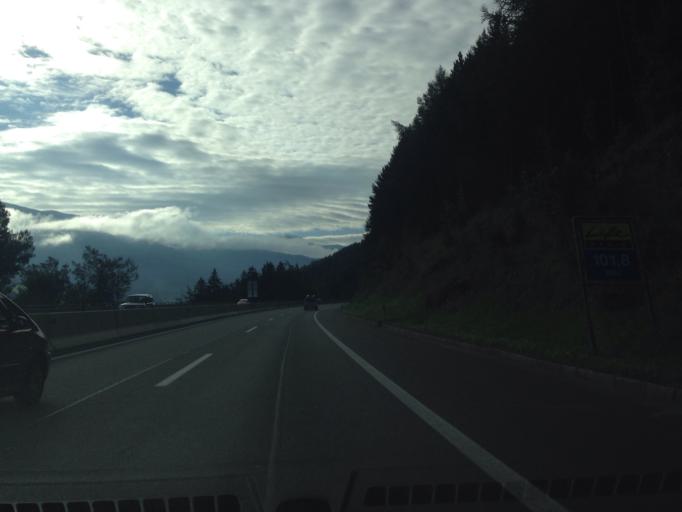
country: AT
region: Tyrol
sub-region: Politischer Bezirk Innsbruck Land
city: Schoenberg im Stubaital
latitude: 47.1797
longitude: 11.4130
